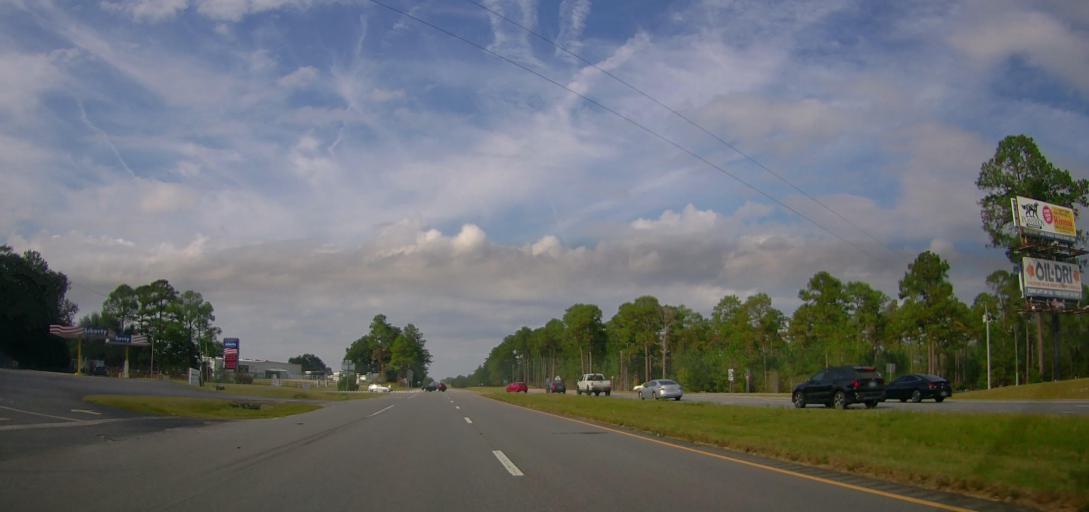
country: US
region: Georgia
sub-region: Thomas County
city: Meigs
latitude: 30.9761
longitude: -84.0367
